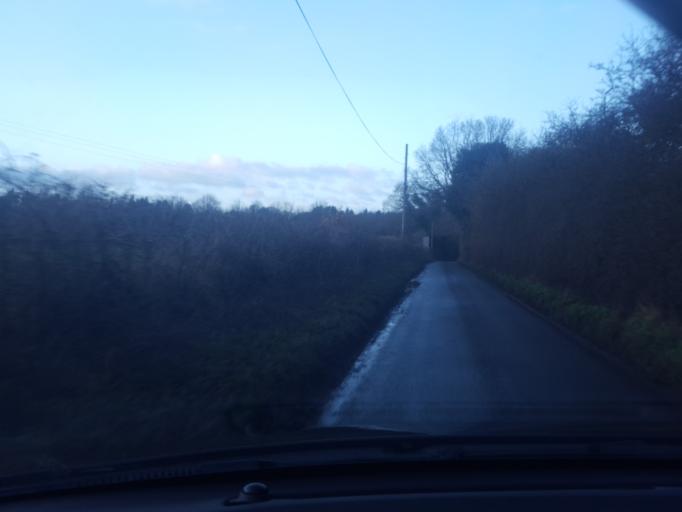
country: GB
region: England
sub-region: Shropshire
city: Tong
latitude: 52.6560
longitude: -2.3164
